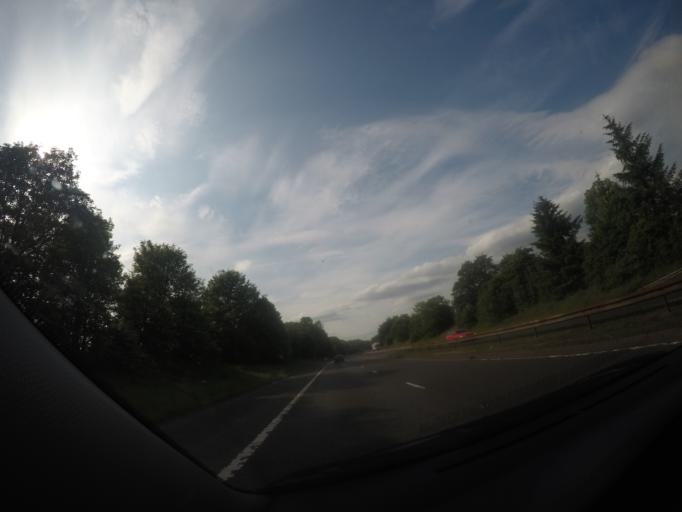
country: GB
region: Scotland
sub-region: South Lanarkshire
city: Larkhall
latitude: 55.7451
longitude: -3.9604
